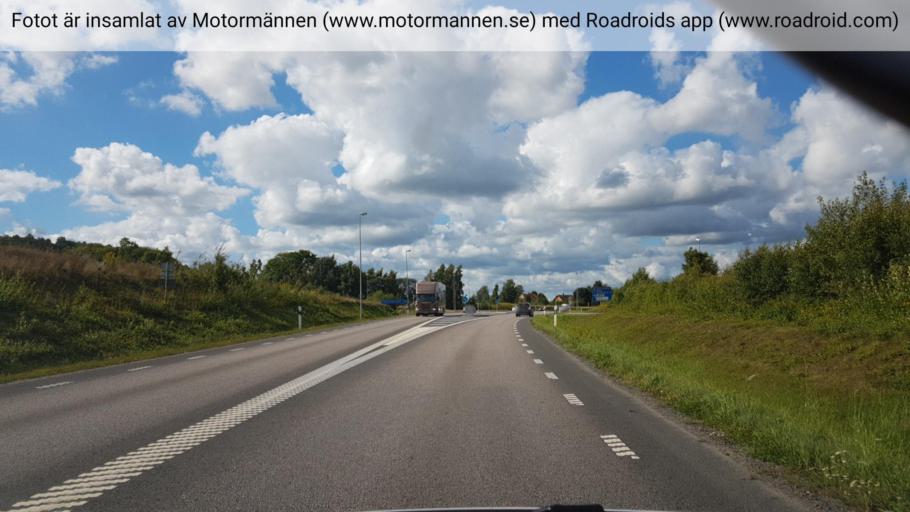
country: SE
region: Vaestra Goetaland
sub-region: Falkopings Kommun
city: Falkoeping
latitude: 58.1885
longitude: 13.5626
